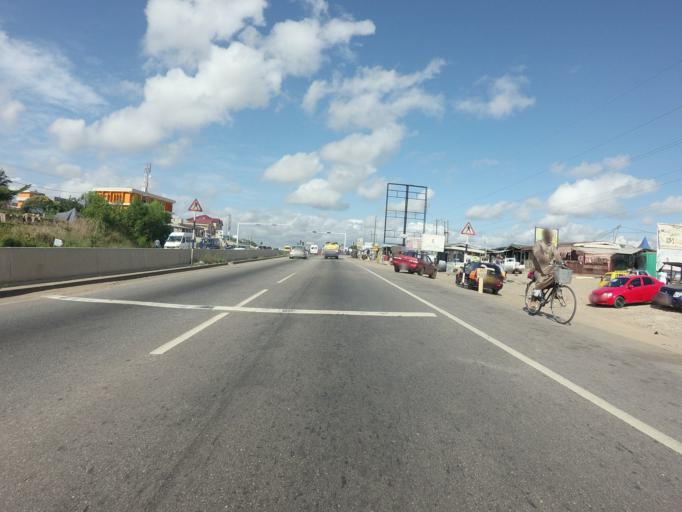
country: GH
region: Central
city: Kasoa
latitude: 5.5325
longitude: -0.4395
